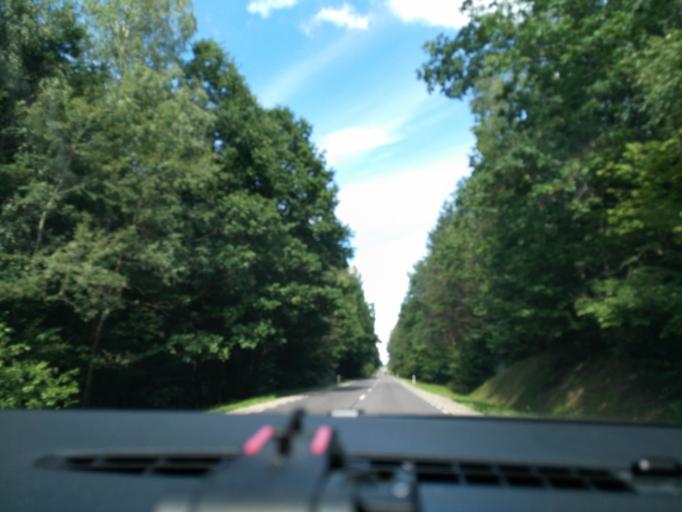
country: PL
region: Podlasie
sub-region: Powiat sejnenski
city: Sejny
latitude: 54.0176
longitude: 23.3367
